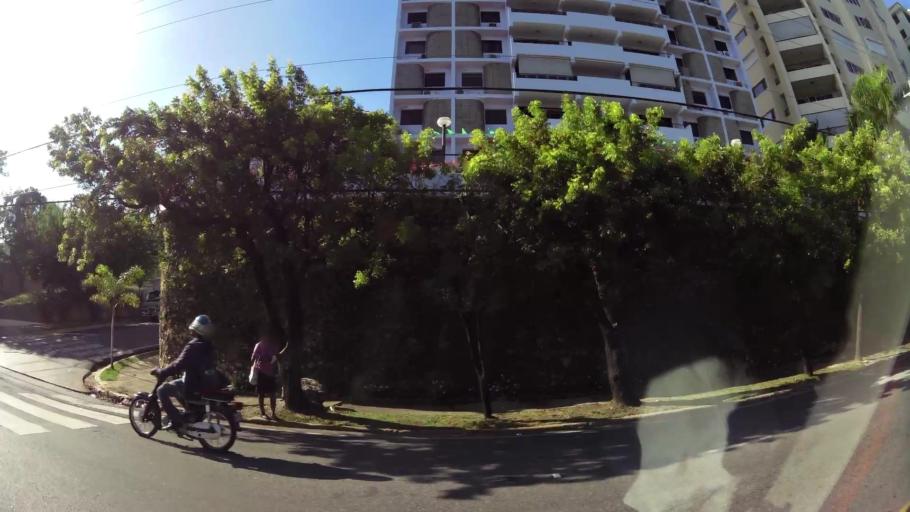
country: DO
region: Nacional
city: Bella Vista
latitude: 18.4391
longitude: -69.9679
